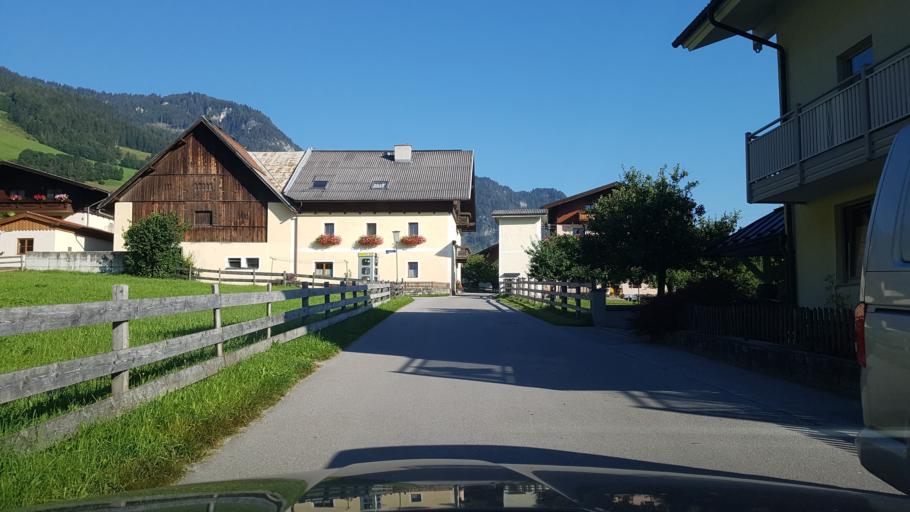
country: AT
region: Salzburg
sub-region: Politischer Bezirk Sankt Johann im Pongau
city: Dorfgastein
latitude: 47.2567
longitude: 13.0841
